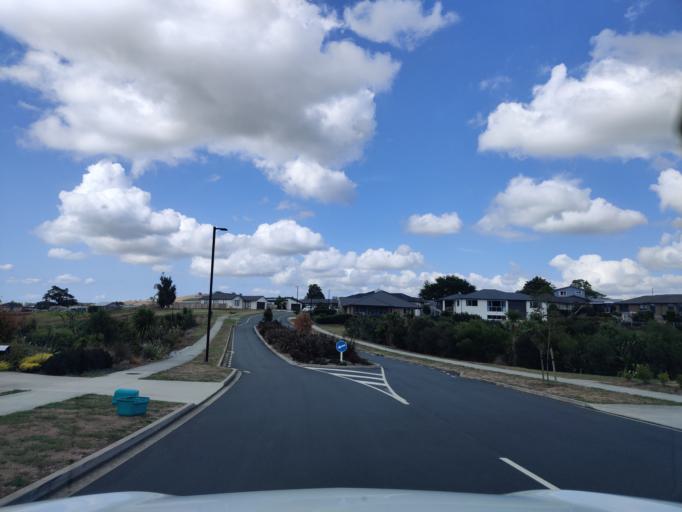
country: NZ
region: Auckland
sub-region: Auckland
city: Pukekohe East
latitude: -37.2403
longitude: 175.0161
